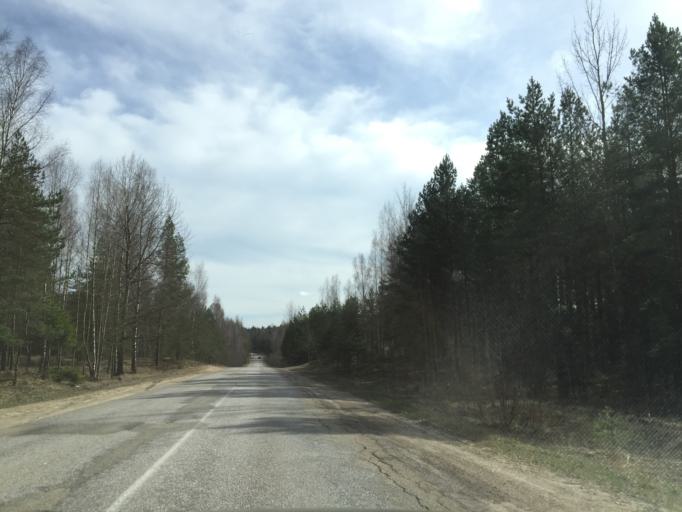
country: LV
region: Ogre
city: Ogre
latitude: 56.8421
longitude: 24.5749
